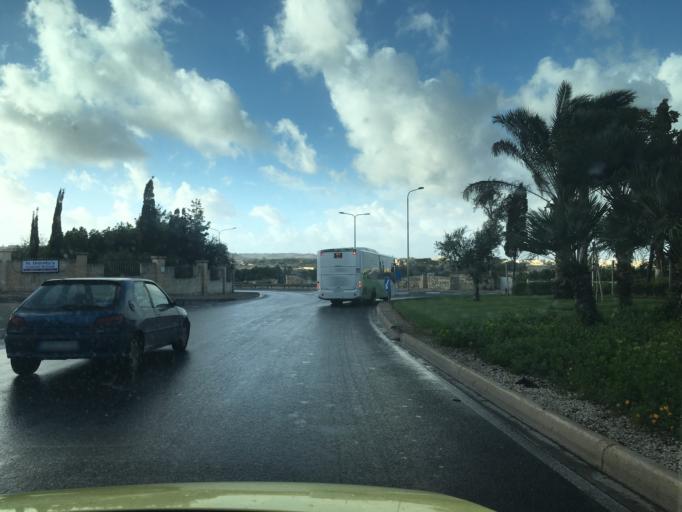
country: MT
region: Haz-Zebbug
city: Haz-Zebbug
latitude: 35.8787
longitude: 14.4386
